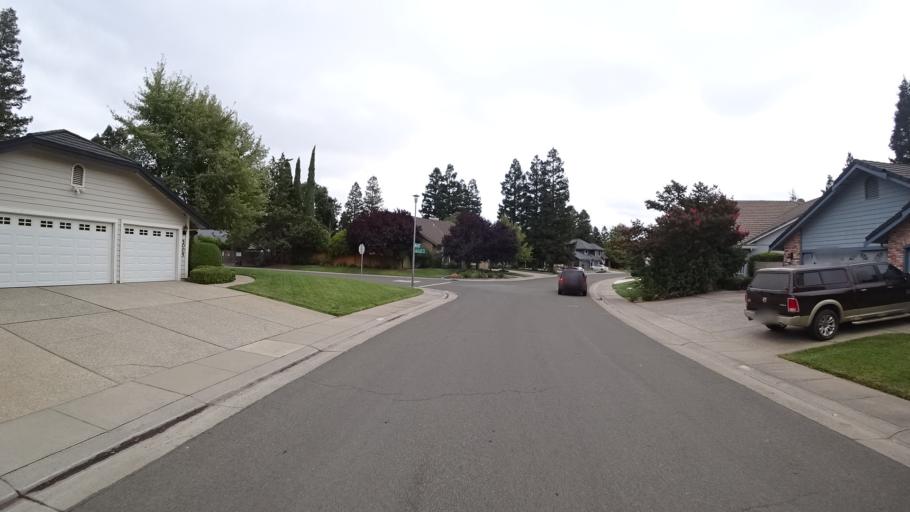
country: US
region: California
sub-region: Sacramento County
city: Laguna
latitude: 38.4192
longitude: -121.4442
